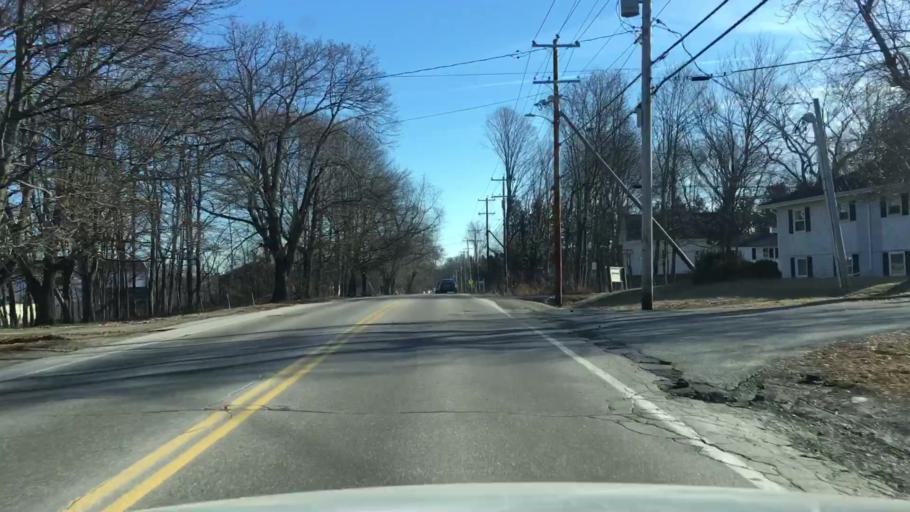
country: US
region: Maine
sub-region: Penobscot County
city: Bangor
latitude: 44.8192
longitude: -68.8025
